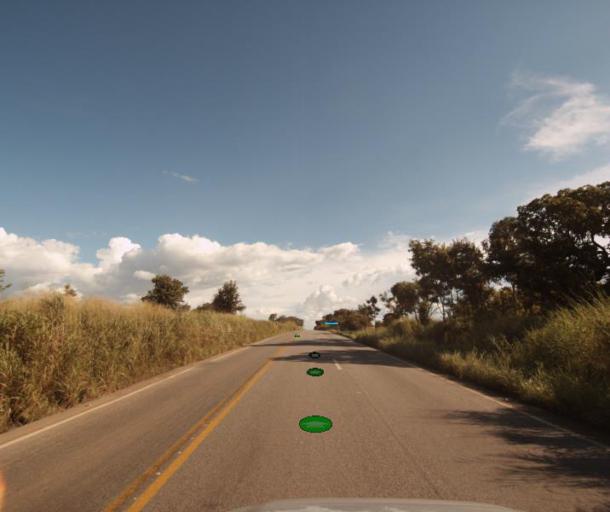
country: BR
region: Goias
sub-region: Porangatu
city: Porangatu
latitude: -13.0736
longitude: -49.1869
